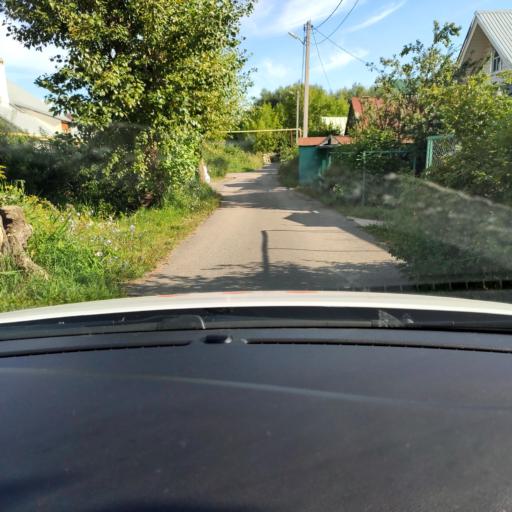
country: RU
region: Tatarstan
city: Verkhniy Uslon
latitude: 55.8013
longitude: 49.0372
